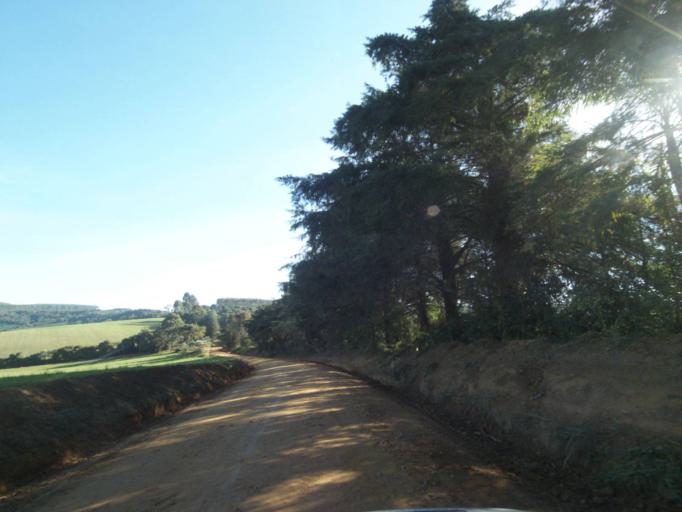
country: BR
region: Parana
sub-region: Tibagi
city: Tibagi
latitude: -24.5332
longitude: -50.5198
